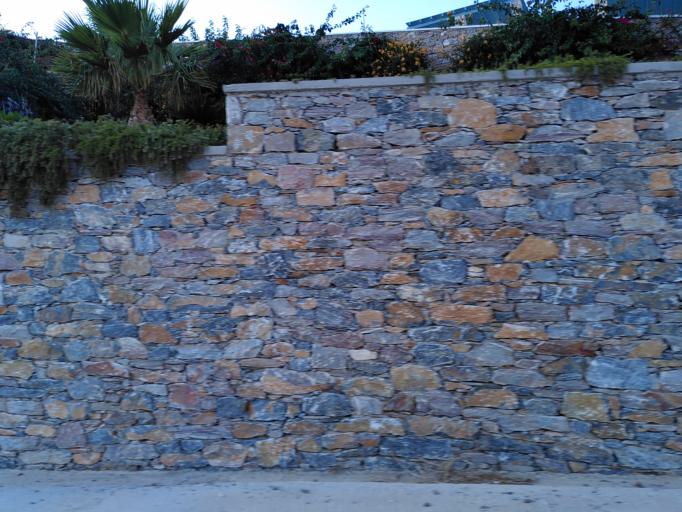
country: GR
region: South Aegean
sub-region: Nomos Kykladon
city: Amorgos
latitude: 36.9148
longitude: 25.9806
